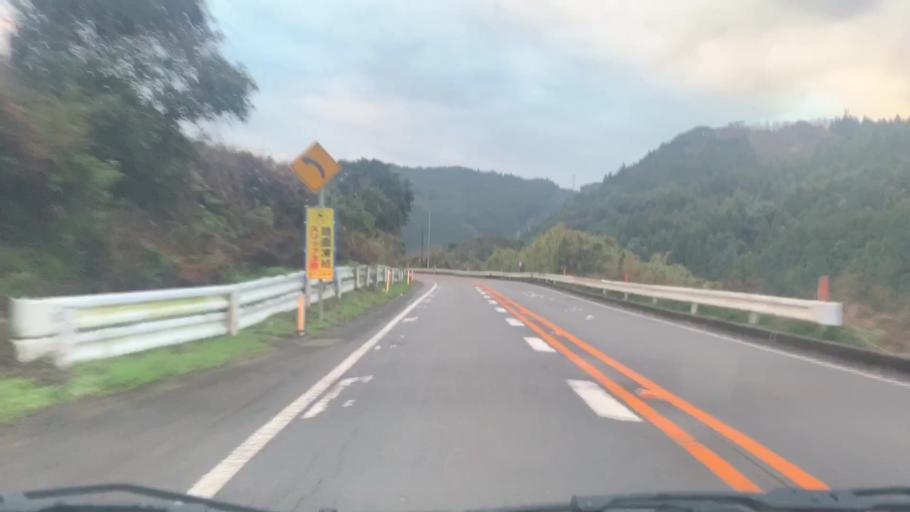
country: JP
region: Saga Prefecture
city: Ureshinomachi-shimojuku
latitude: 33.0715
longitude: 129.9613
